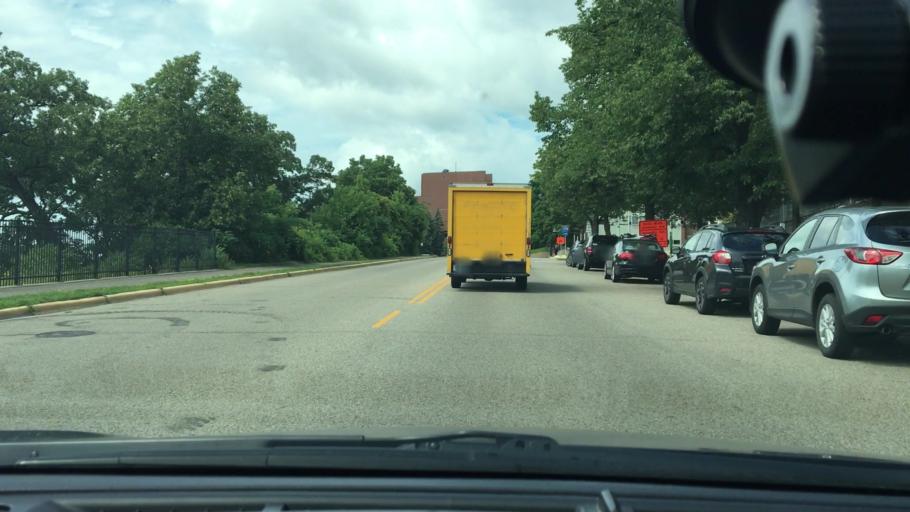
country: US
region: Minnesota
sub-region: Hennepin County
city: Minneapolis
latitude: 44.9747
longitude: -93.2379
